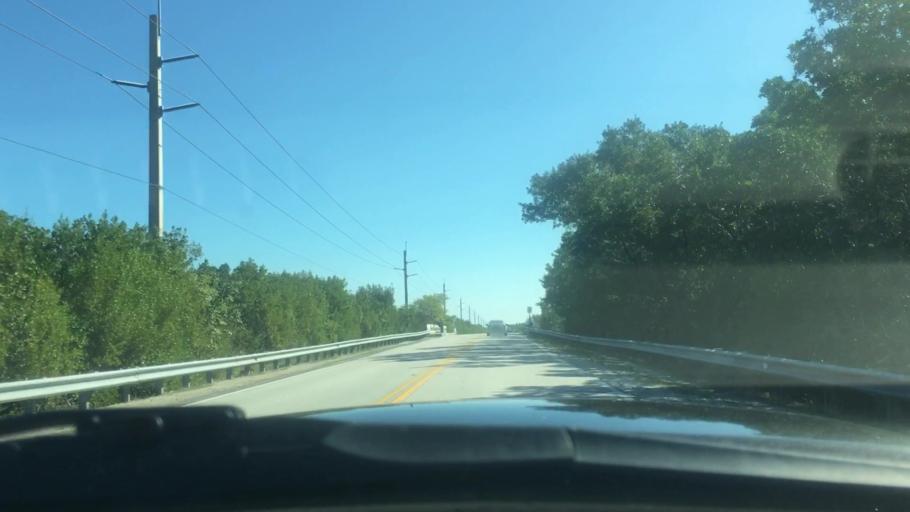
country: US
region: Florida
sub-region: Monroe County
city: North Key Largo
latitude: 25.2829
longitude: -80.3552
